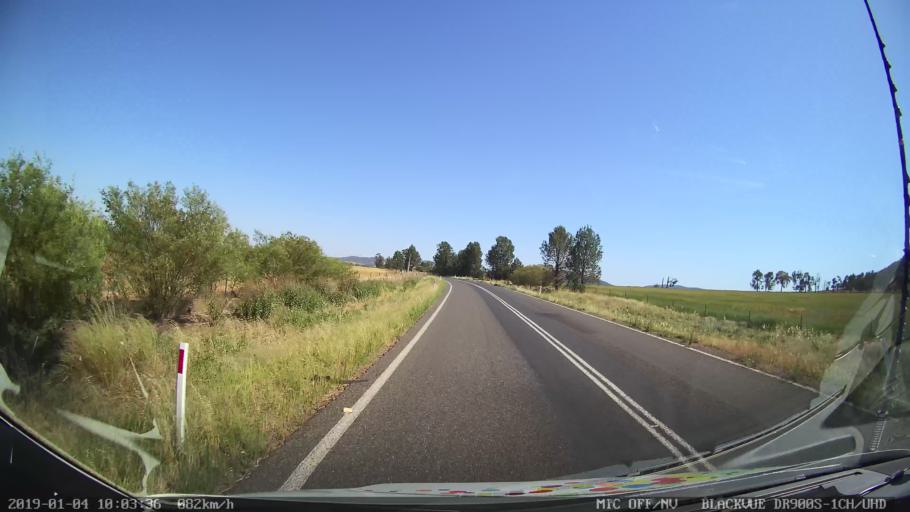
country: AU
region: New South Wales
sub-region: Cabonne
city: Canowindra
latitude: -33.4619
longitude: 148.3641
